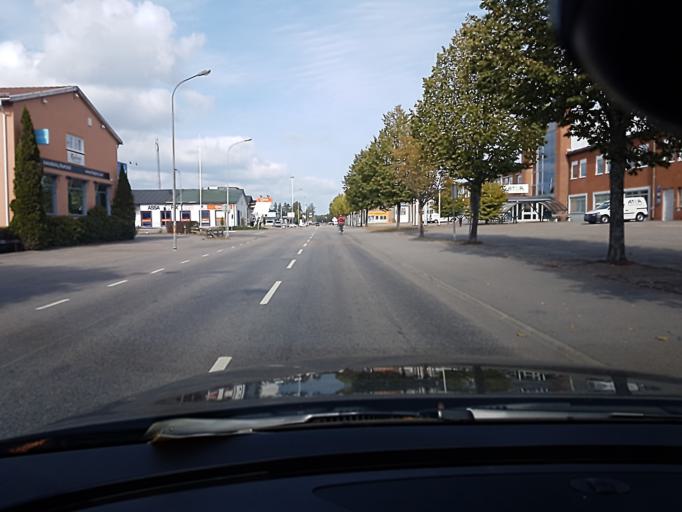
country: SE
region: Kronoberg
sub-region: Vaxjo Kommun
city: Vaexjoe
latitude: 56.8826
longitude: 14.7803
